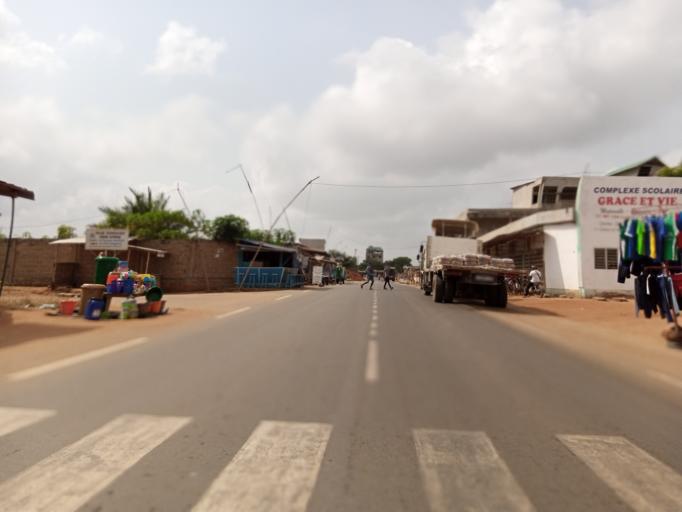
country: TG
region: Maritime
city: Lome
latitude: 6.2333
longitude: 1.0977
